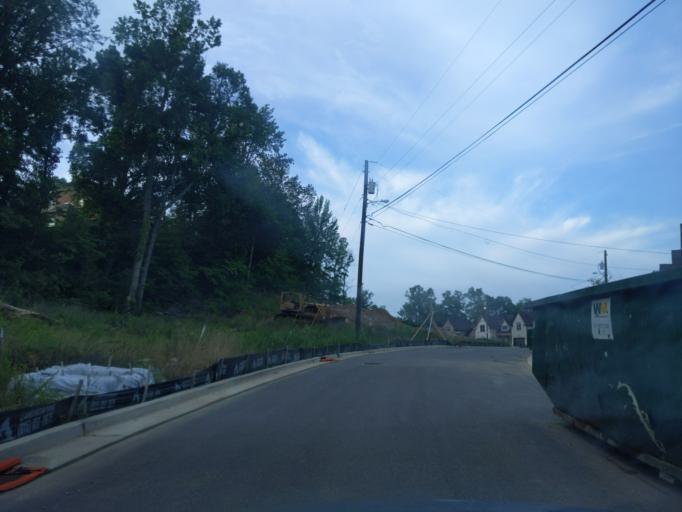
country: US
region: Tennessee
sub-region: Wilson County
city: Green Hill
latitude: 36.1810
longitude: -86.5988
